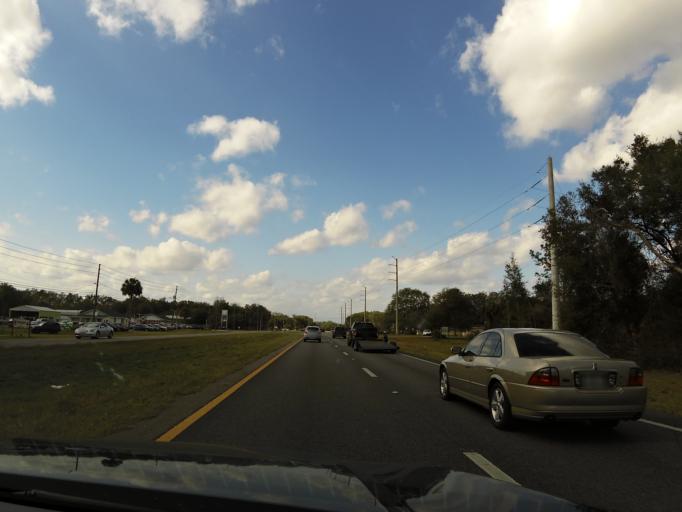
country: US
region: Florida
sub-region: Volusia County
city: North DeLand
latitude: 29.0761
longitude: -81.3111
